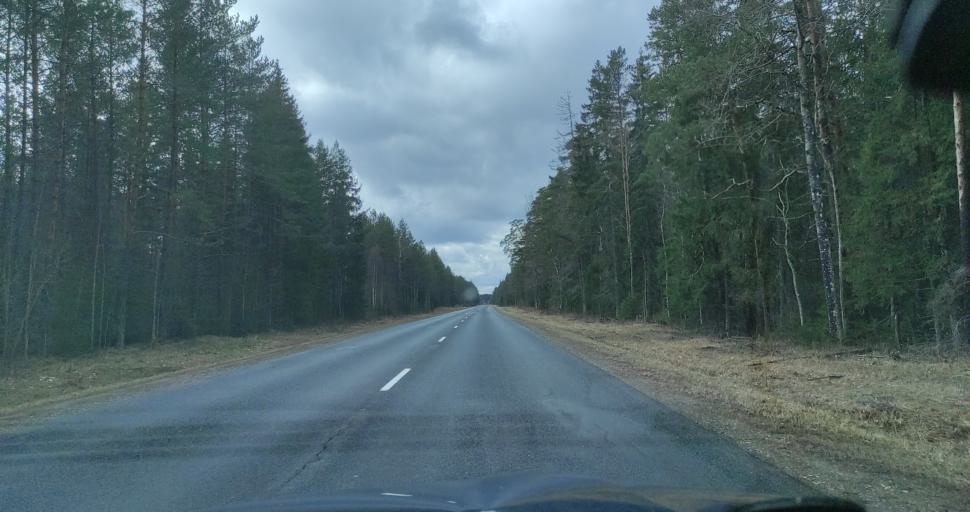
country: LV
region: Talsu Rajons
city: Stende
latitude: 57.1130
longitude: 22.5057
